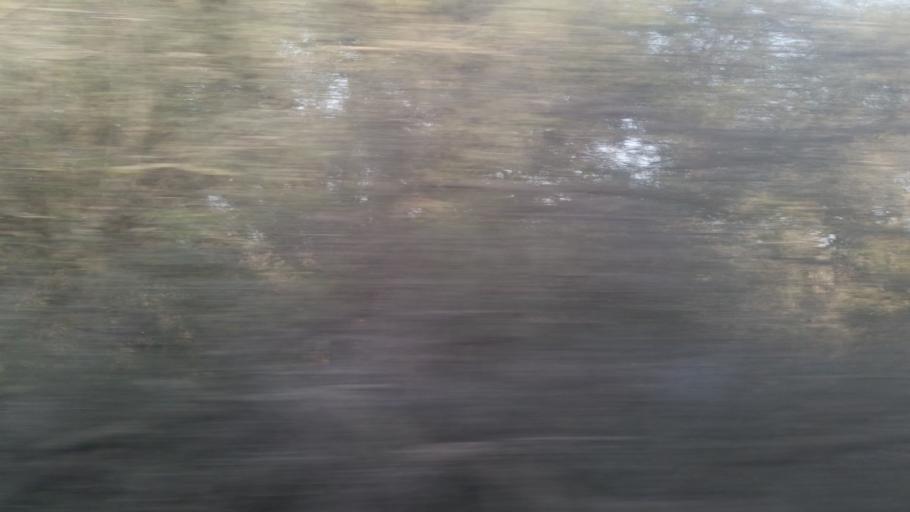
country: AR
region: Cordoba
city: Bell Ville
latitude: -32.6300
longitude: -62.4934
